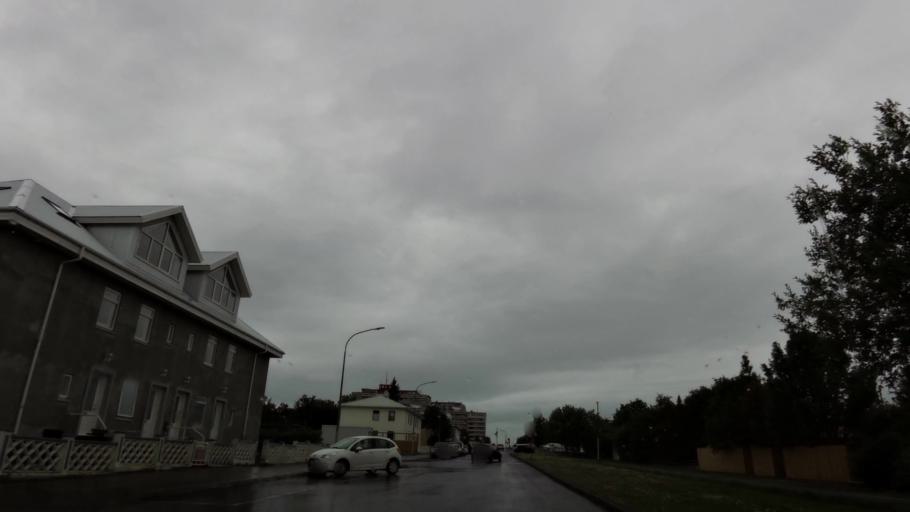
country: IS
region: Capital Region
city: Reykjavik
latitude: 64.1241
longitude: -21.8751
